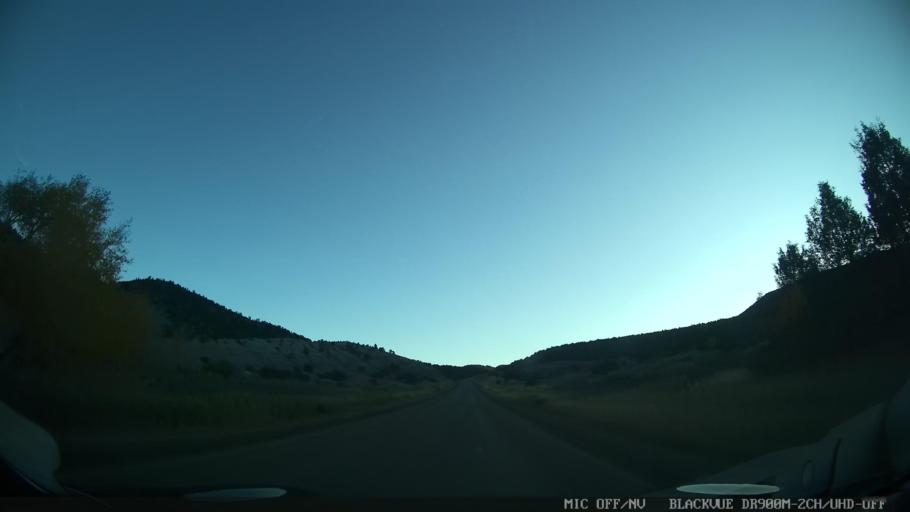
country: US
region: Colorado
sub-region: Grand County
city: Kremmling
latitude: 39.9035
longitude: -106.5890
